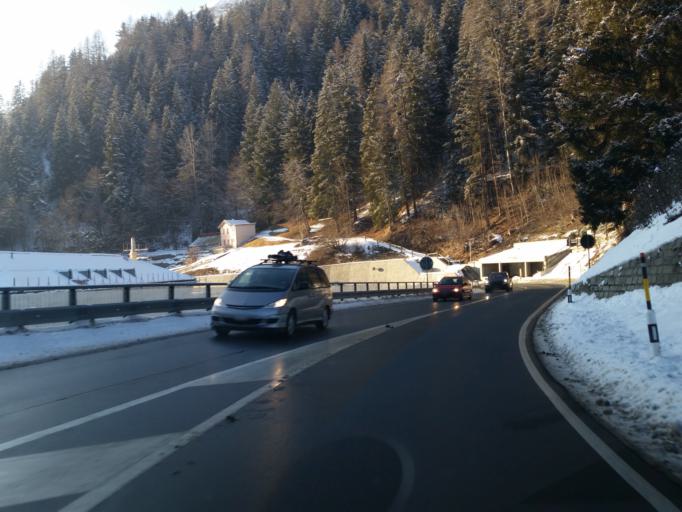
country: CH
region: Grisons
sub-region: Inn District
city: Scuol
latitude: 46.7895
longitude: 10.2775
